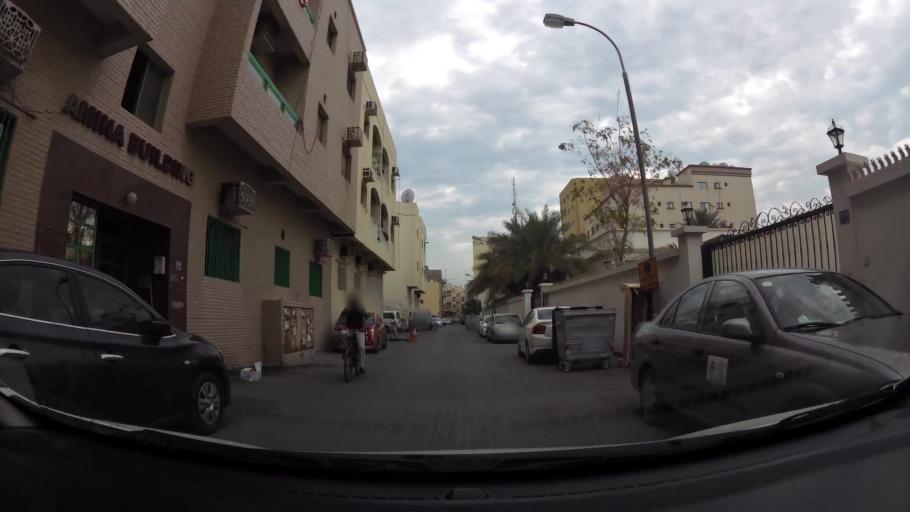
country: BH
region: Manama
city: Manama
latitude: 26.2244
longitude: 50.5899
